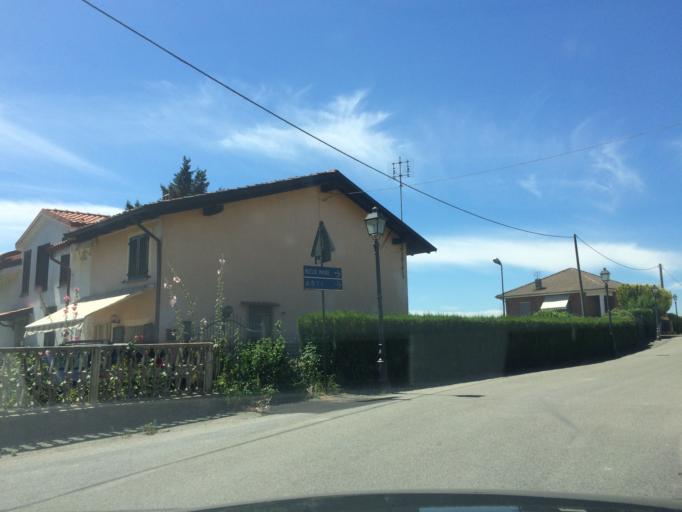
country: IT
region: Piedmont
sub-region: Provincia di Asti
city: Castel Rocchero
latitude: 44.7202
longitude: 8.4150
